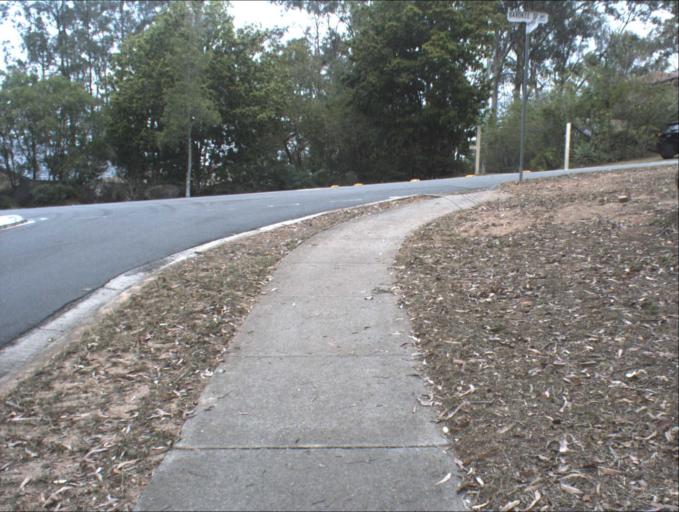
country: AU
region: Queensland
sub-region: Logan
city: Slacks Creek
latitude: -27.6741
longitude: 153.1762
